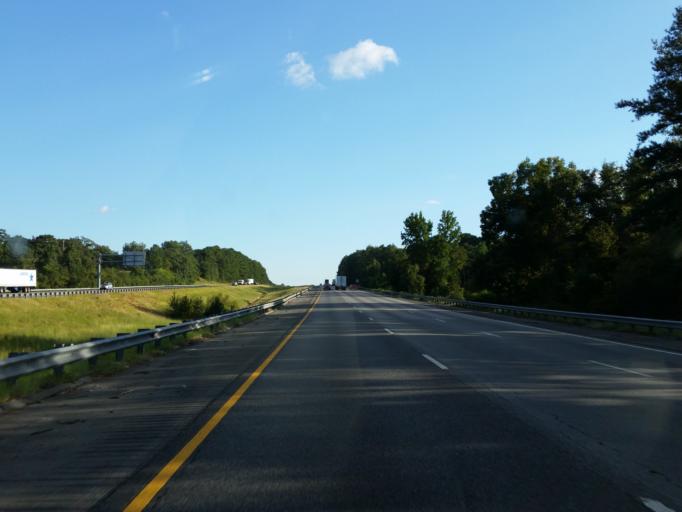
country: US
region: Georgia
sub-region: Houston County
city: Perry
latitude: 32.5301
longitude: -83.7438
